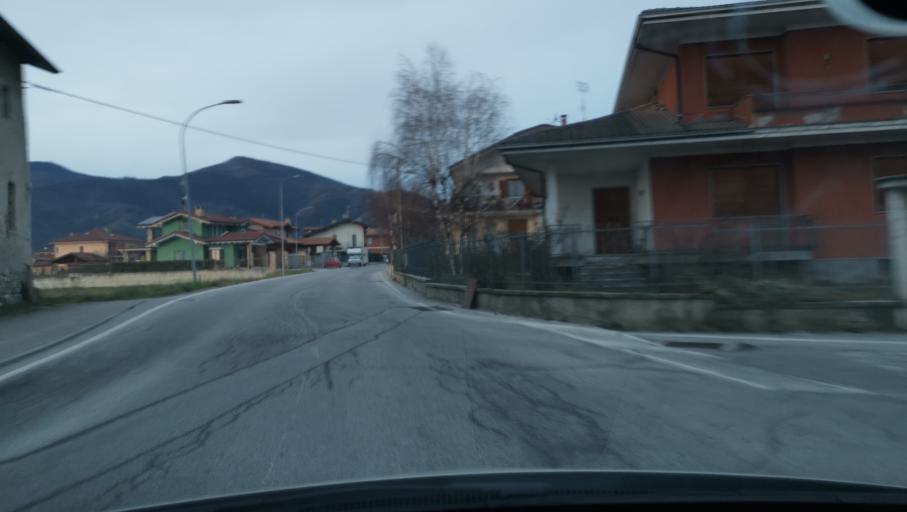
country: IT
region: Piedmont
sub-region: Provincia di Cuneo
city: Caraglio
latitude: 44.4144
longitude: 7.4322
